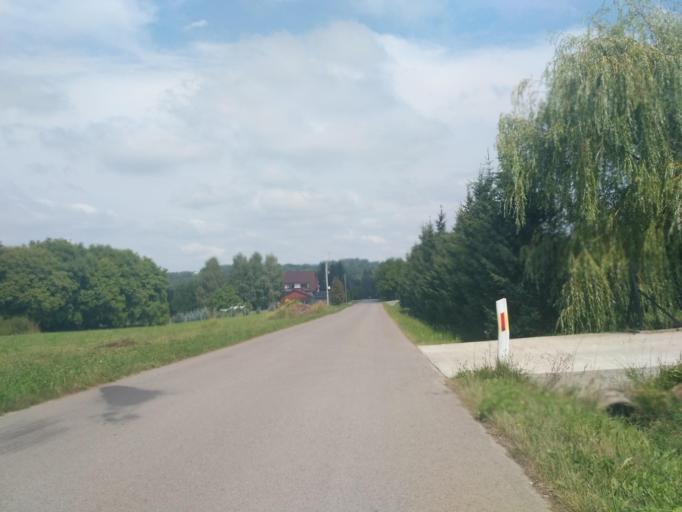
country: PL
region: Subcarpathian Voivodeship
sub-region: Powiat lancucki
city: Kraczkowa
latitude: 50.0325
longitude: 22.1670
